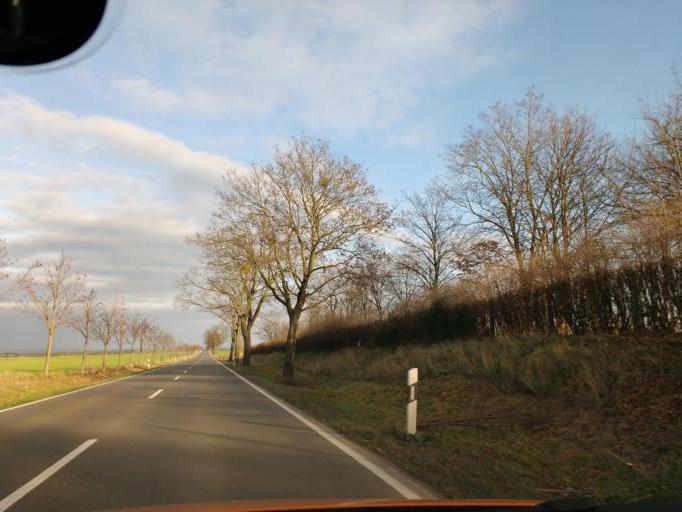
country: DE
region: Brandenburg
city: Wriezen
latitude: 52.6924
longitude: 14.1042
